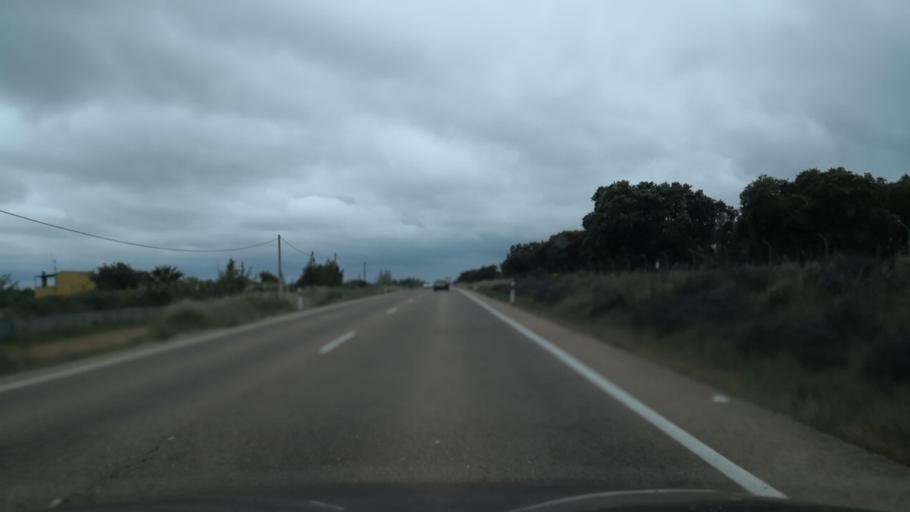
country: ES
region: Extremadura
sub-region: Provincia de Badajoz
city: Villar del Rey
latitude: 39.0051
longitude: -6.8615
